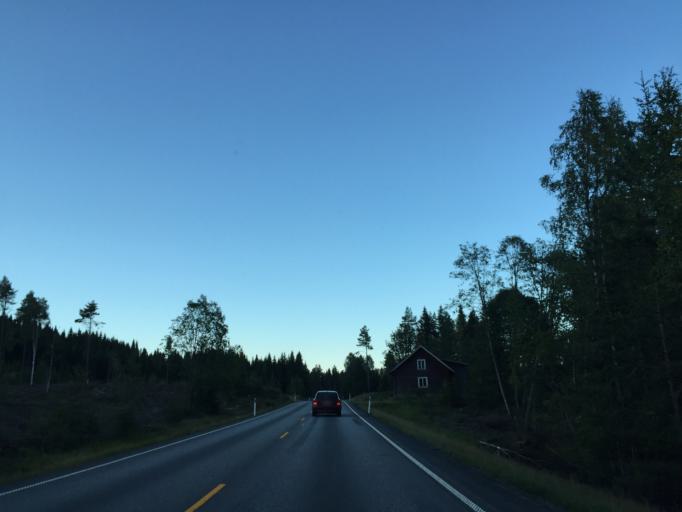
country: NO
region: Hedmark
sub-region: Nord-Odal
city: Sand
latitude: 60.4912
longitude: 11.5005
